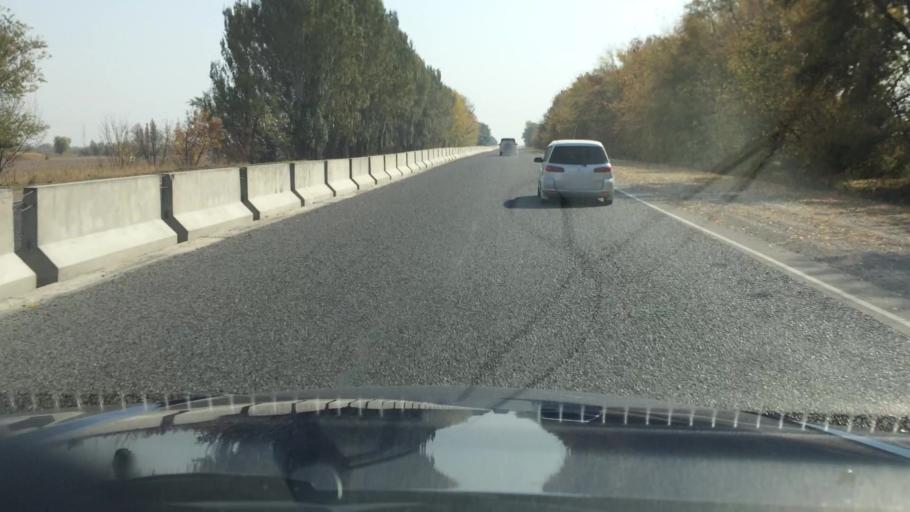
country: KG
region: Chuy
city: Kant
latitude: 42.9647
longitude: 74.9136
